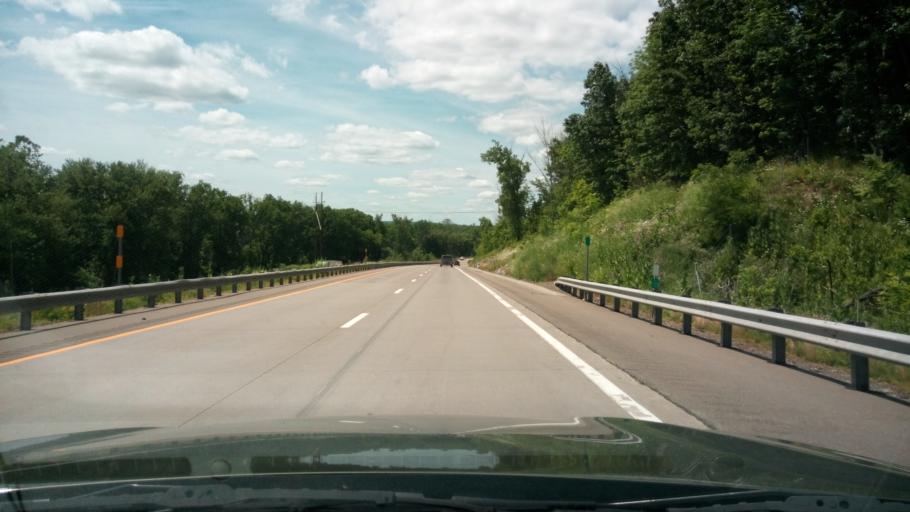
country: US
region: New York
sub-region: Chemung County
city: Elmira
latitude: 42.0570
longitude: -76.7553
